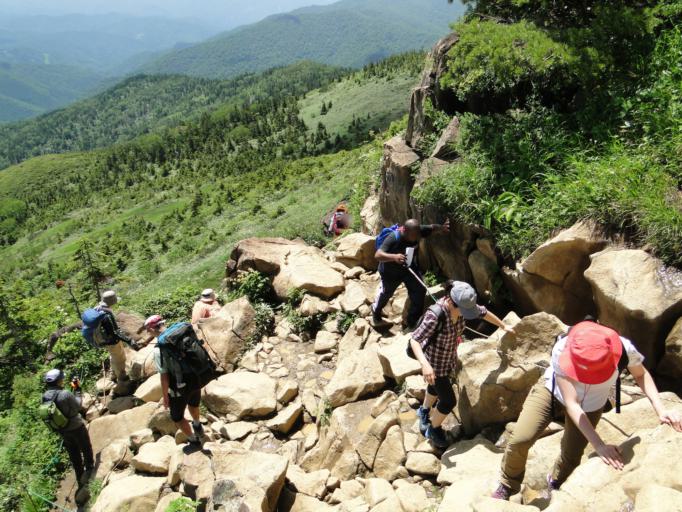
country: JP
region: Gunma
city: Numata
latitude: 36.8942
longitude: 139.1724
